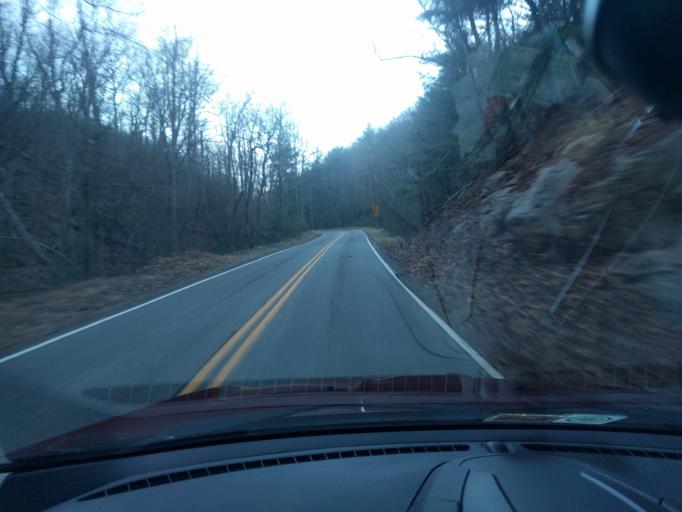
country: US
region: Virginia
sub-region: Botetourt County
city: Buchanan
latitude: 37.4903
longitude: -79.6630
